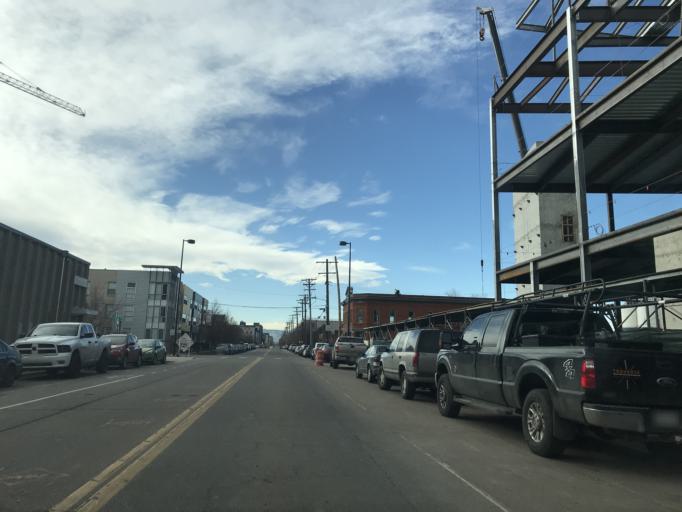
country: US
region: Colorado
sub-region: Denver County
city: Denver
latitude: 39.7688
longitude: -104.9757
